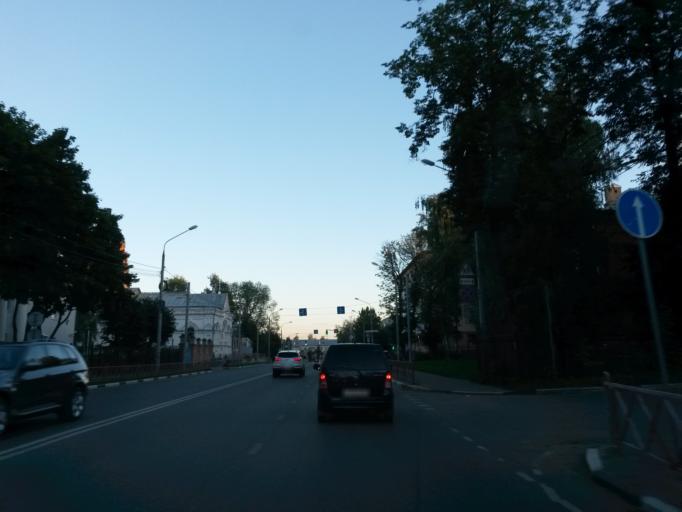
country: RU
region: Jaroslavl
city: Yaroslavl
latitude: 57.6246
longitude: 39.8679
